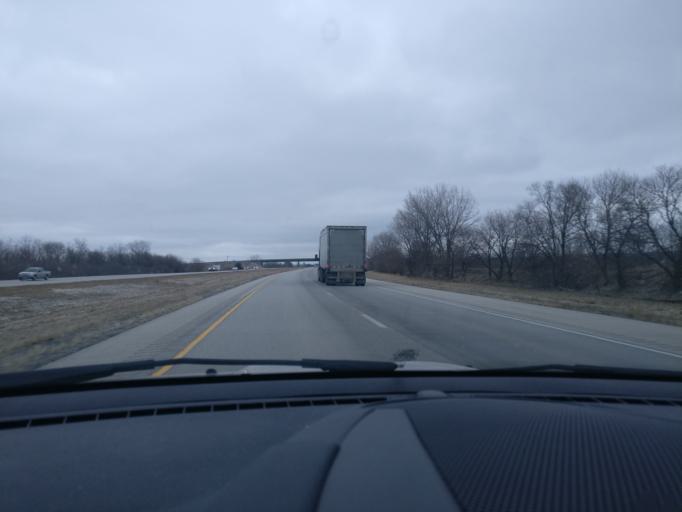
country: US
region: Iowa
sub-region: Scott County
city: Le Claire
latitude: 41.5412
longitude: -90.2825
